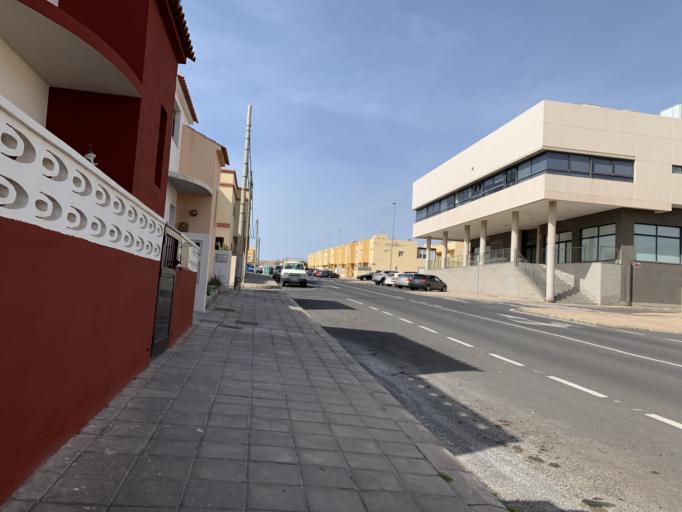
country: ES
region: Canary Islands
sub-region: Provincia de Las Palmas
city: Puerto del Rosario
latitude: 28.5095
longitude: -13.8588
